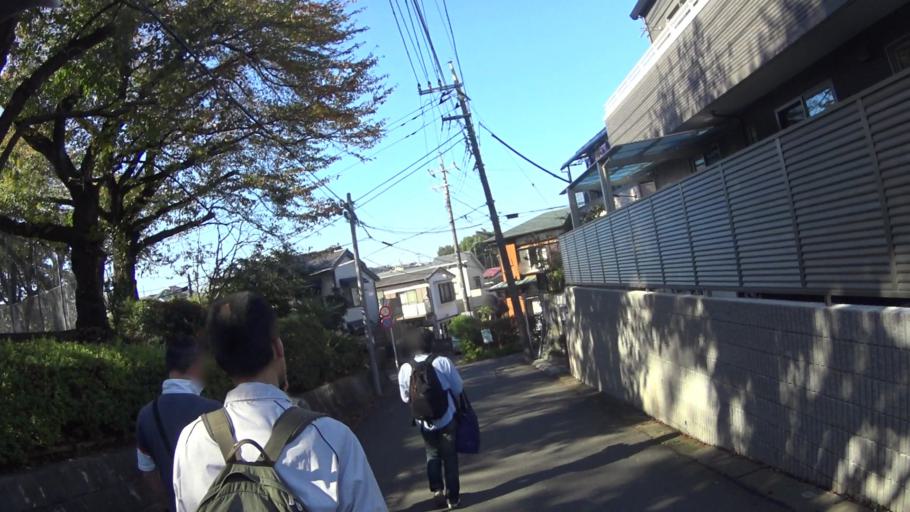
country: JP
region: Tokyo
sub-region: Machida-shi
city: Machida
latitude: 35.5580
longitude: 139.4469
